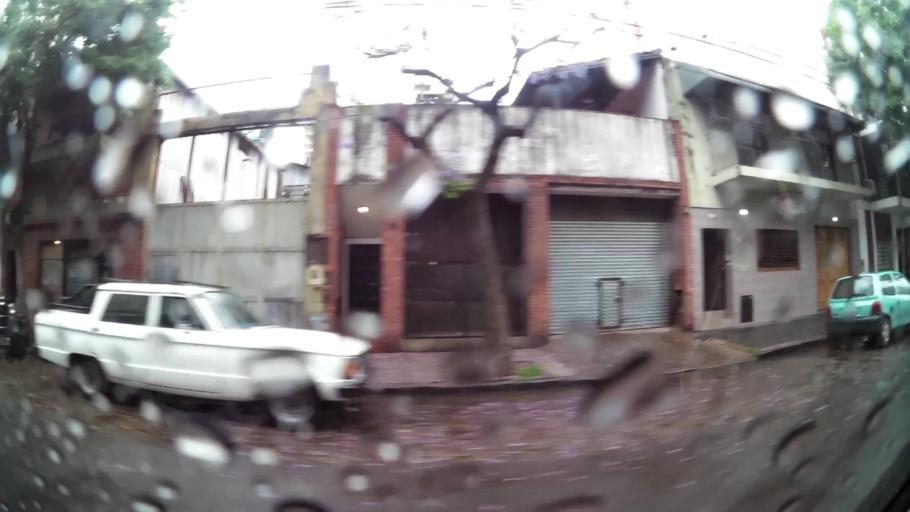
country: AR
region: Buenos Aires
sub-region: Partido de Avellaneda
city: Avellaneda
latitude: -34.6438
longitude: -58.3724
